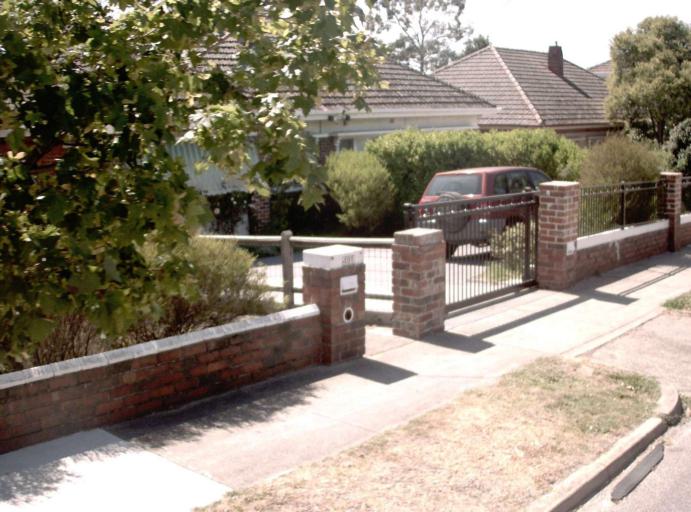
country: AU
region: Victoria
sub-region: Boroondara
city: Camberwell
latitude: -37.8412
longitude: 145.0681
